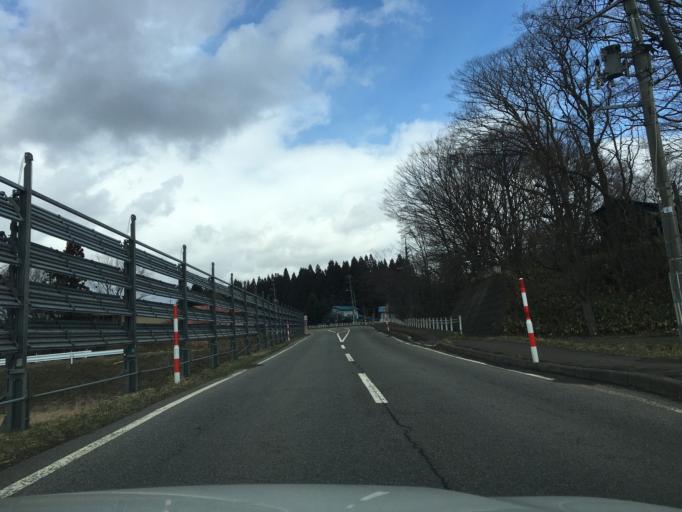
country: JP
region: Akita
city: Takanosu
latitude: 40.1535
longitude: 140.3353
